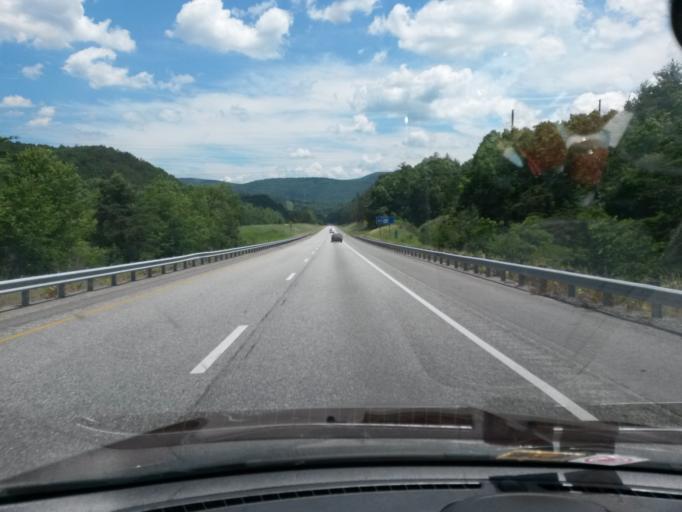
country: US
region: Virginia
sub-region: City of Covington
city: Covington
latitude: 37.7813
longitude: -80.0082
